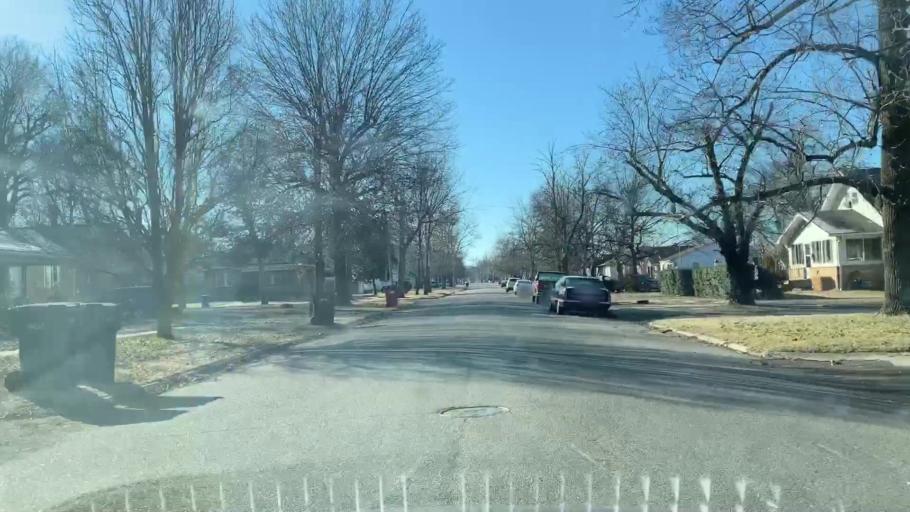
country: US
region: Kansas
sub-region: Cherokee County
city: Baxter Springs
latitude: 37.0189
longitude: -94.7344
